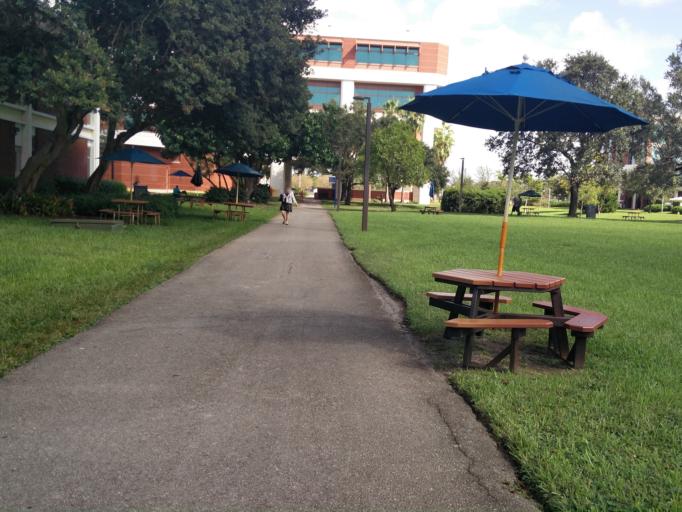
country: US
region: Florida
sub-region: Broward County
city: Davie
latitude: 26.0808
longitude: -80.2353
